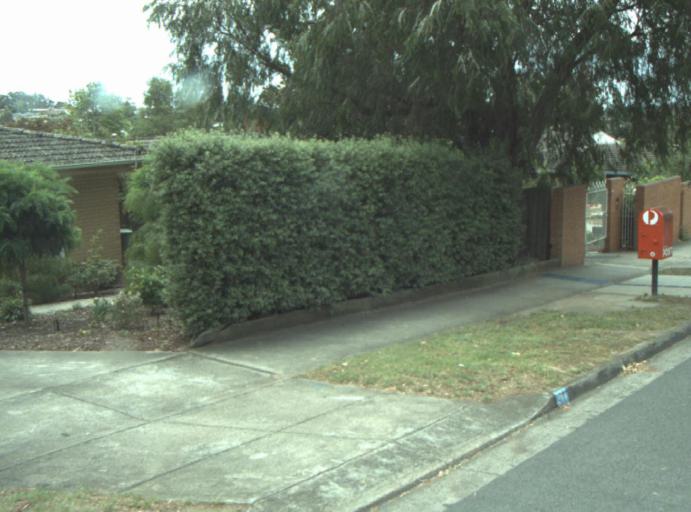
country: AU
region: Victoria
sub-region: Greater Geelong
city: Wandana Heights
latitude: -38.1719
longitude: 144.3142
